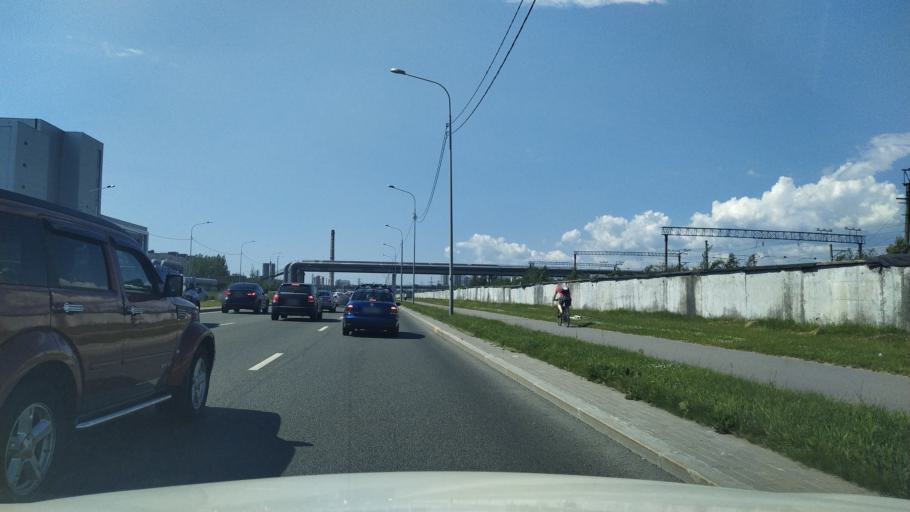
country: RU
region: Leningrad
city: Parnas
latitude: 60.0584
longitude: 30.3523
